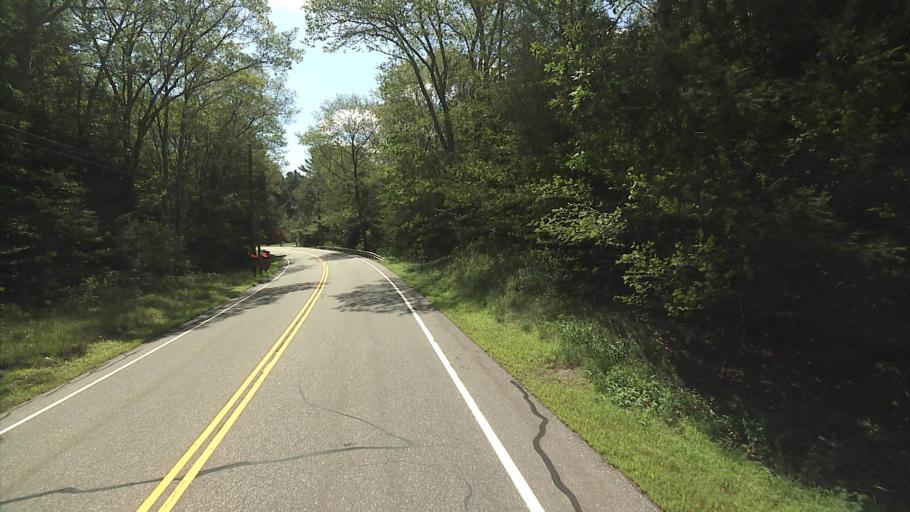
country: US
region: Connecticut
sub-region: Windham County
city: South Woodstock
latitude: 41.9256
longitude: -72.0829
